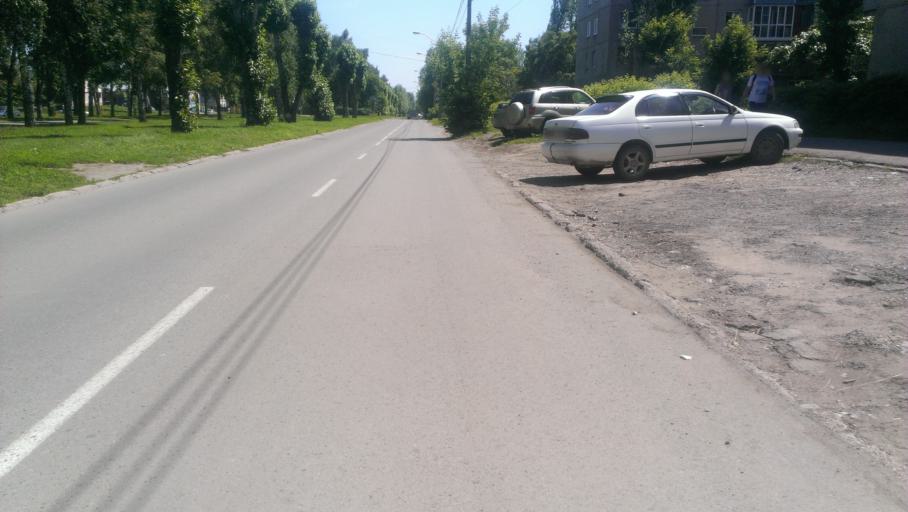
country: RU
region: Altai Krai
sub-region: Gorod Barnaulskiy
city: Barnaul
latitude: 53.3617
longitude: 83.7104
